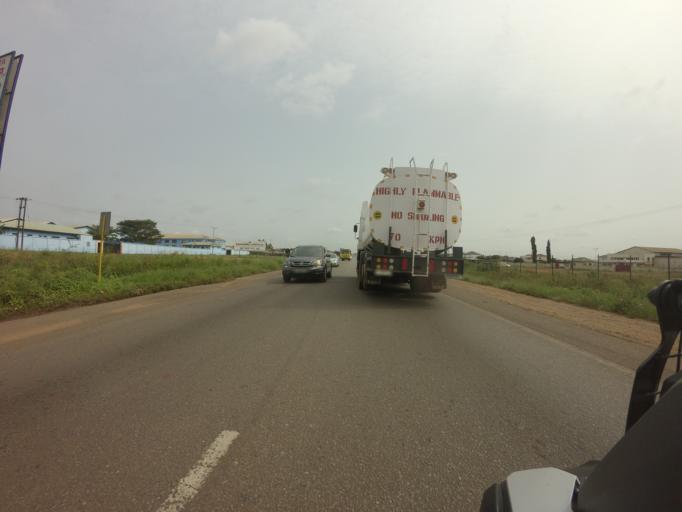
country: GH
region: Greater Accra
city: Tema
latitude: 5.7238
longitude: 0.0210
